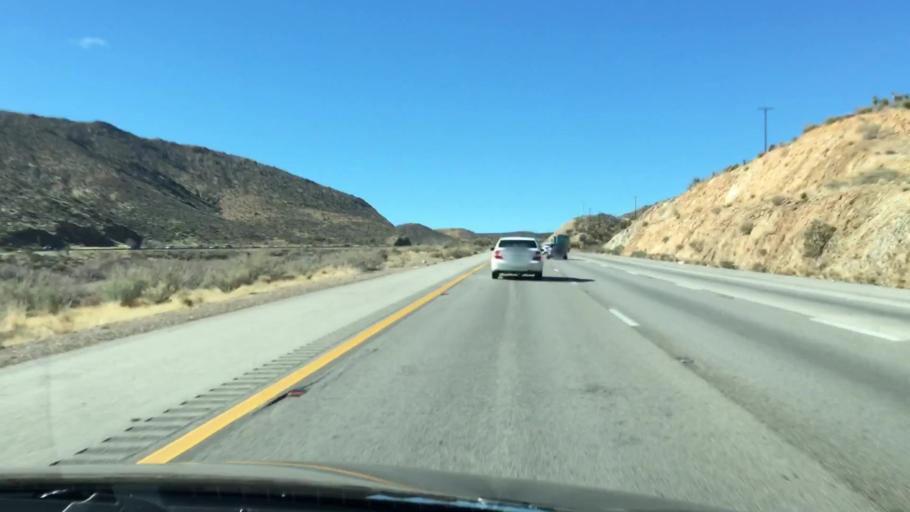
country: US
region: Nevada
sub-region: Clark County
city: Sandy Valley
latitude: 35.4690
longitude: -115.4930
